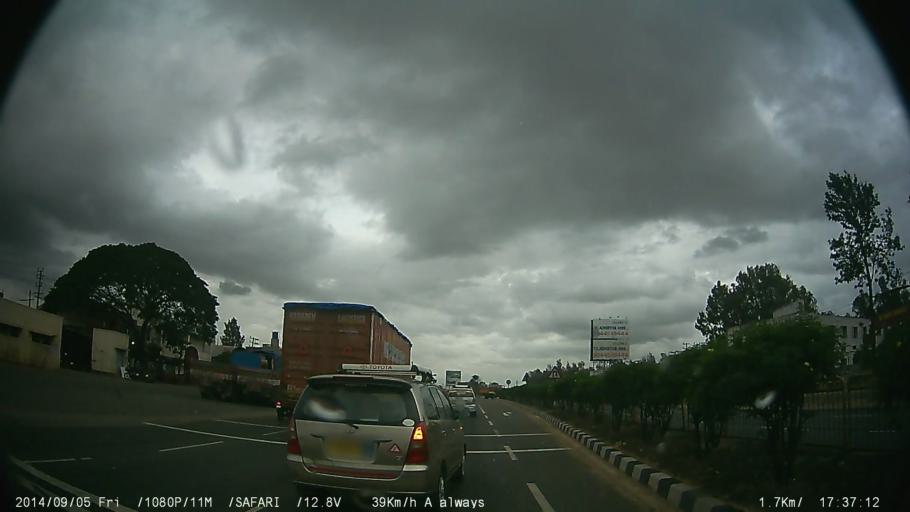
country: IN
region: Karnataka
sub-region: Bangalore Urban
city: Anekal
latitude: 12.8010
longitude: 77.7130
